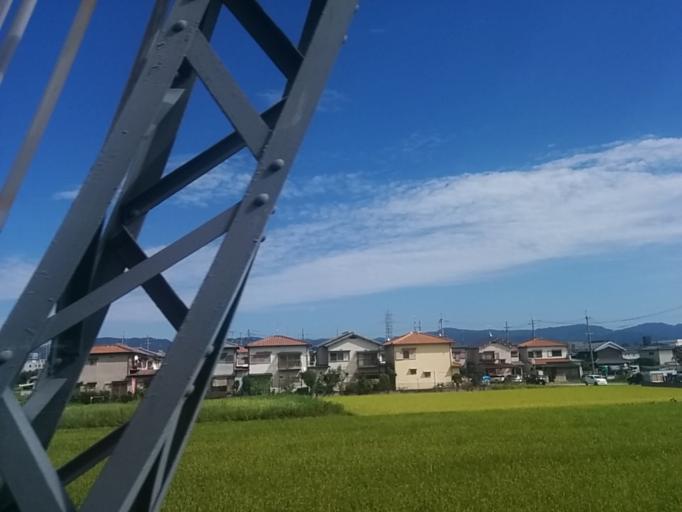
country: JP
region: Nara
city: Nara-shi
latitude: 34.6643
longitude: 135.7839
